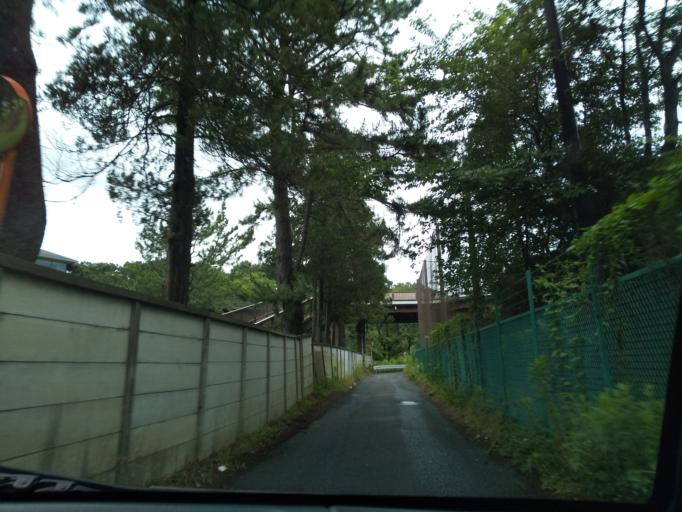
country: JP
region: Kanagawa
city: Minami-rinkan
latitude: 35.4270
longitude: 139.4433
